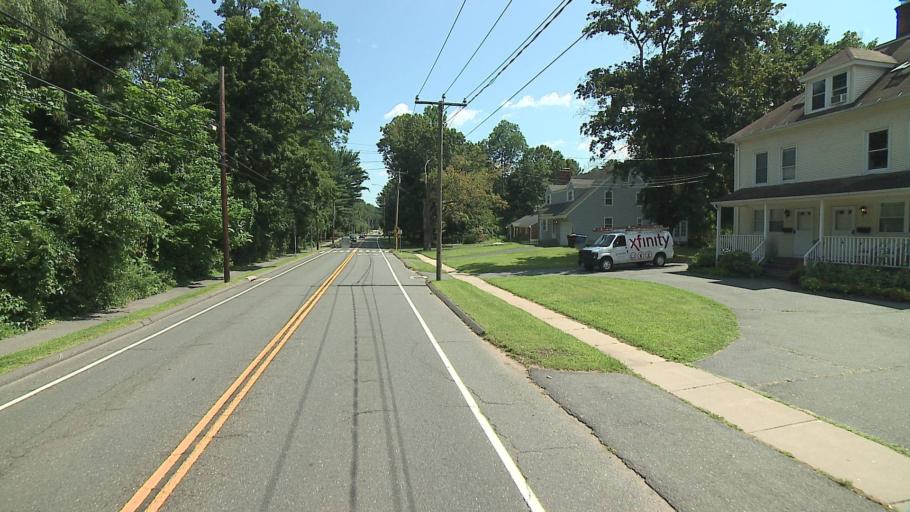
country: US
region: Connecticut
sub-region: Hartford County
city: Farmington
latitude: 41.7529
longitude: -72.8746
